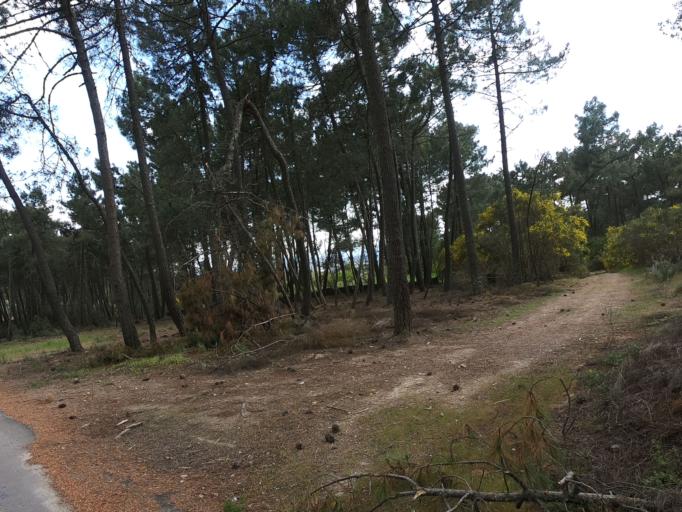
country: PT
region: Vila Real
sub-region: Vila Real
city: Vila Real
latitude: 41.2979
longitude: -7.6882
